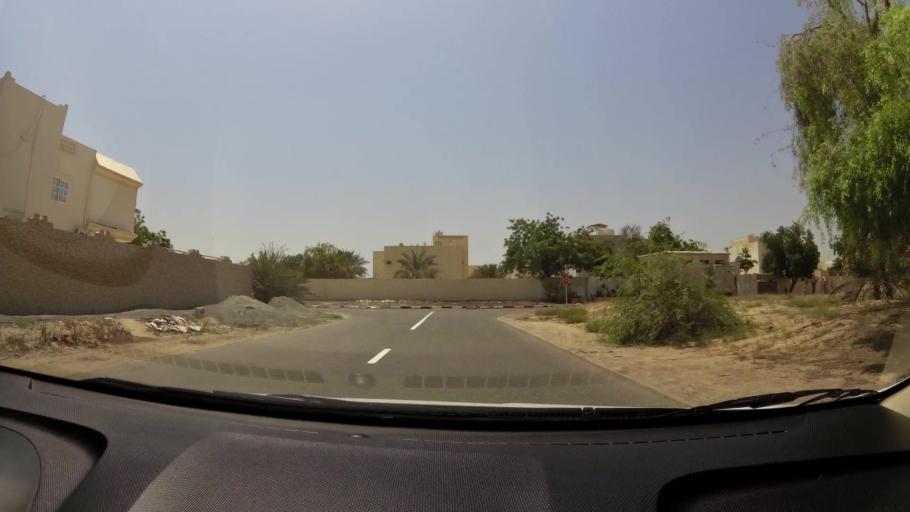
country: AE
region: Ajman
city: Ajman
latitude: 25.4249
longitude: 55.5042
